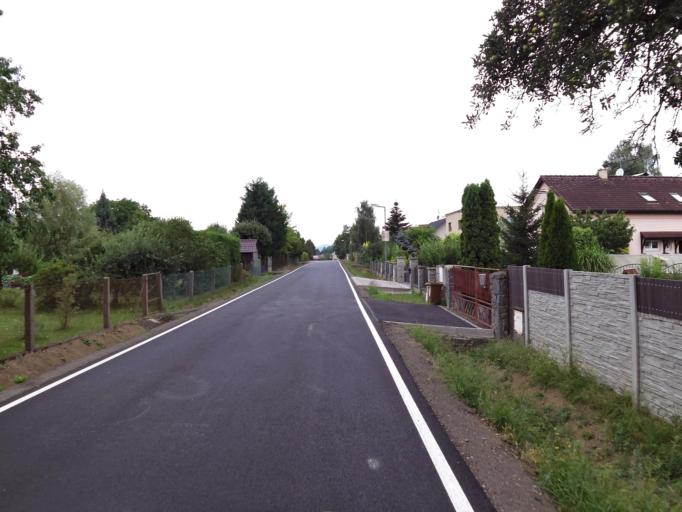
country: CZ
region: Central Bohemia
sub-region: Okres Benesov
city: Pysely
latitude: 49.8733
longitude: 14.6886
